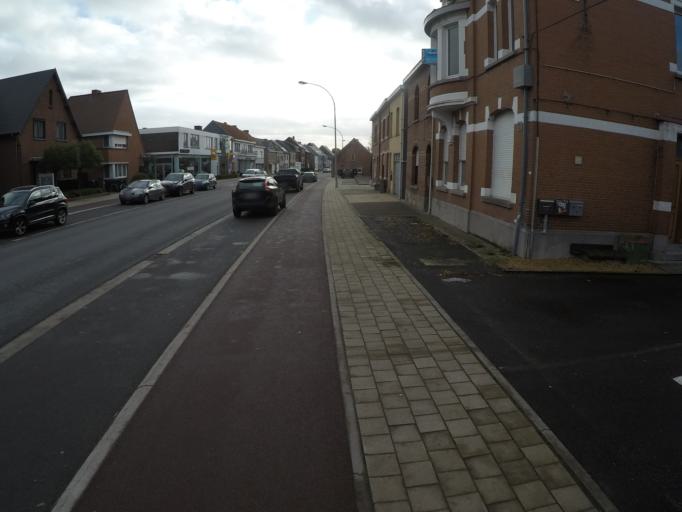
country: BE
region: Flanders
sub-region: Provincie Vlaams-Brabant
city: Londerzeel
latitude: 51.0139
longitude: 4.2958
